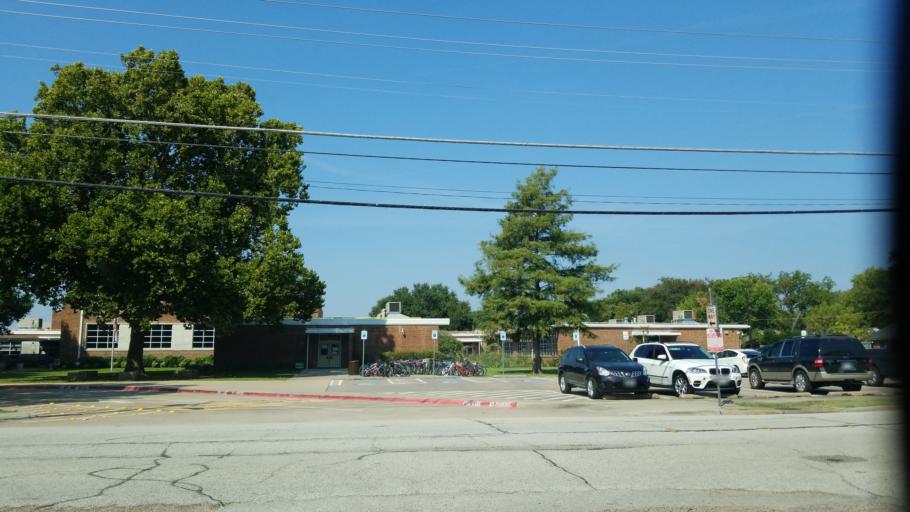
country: US
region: Texas
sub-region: Dallas County
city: Richardson
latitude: 32.9520
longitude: -96.7437
